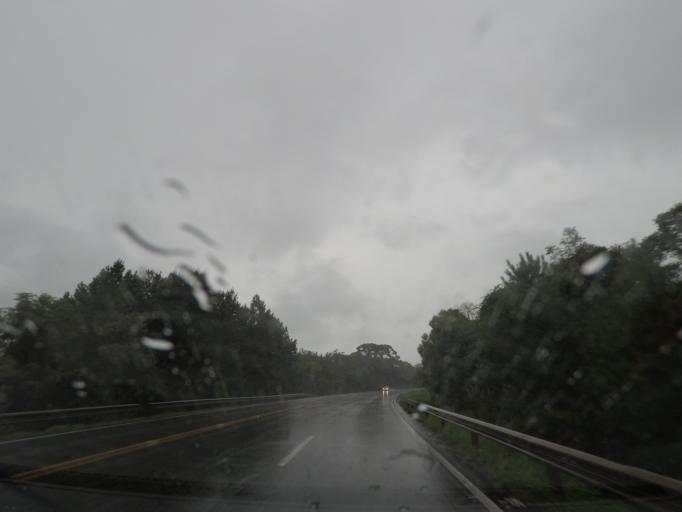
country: BR
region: Parana
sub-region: Almirante Tamandare
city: Almirante Tamandare
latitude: -25.3545
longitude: -49.3070
